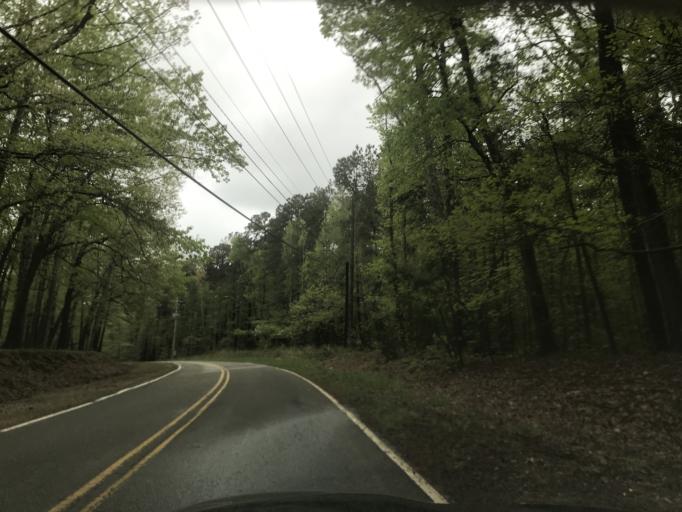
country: US
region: North Carolina
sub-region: Wake County
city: West Raleigh
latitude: 35.7587
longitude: -78.7047
